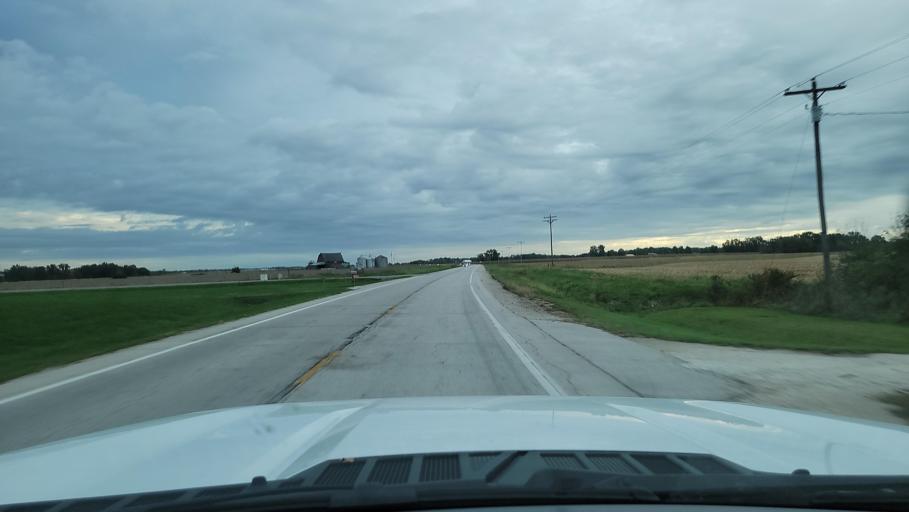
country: US
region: Illinois
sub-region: Schuyler County
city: Rushville
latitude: 40.0941
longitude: -90.6046
